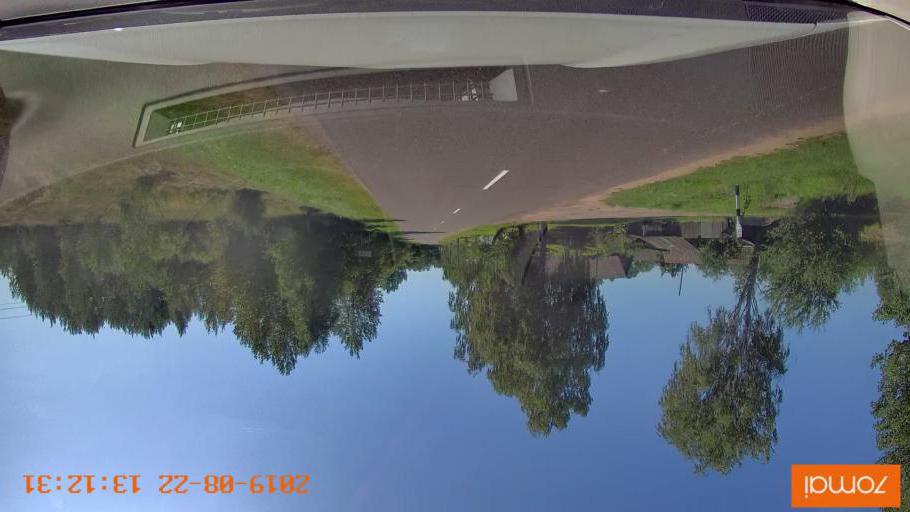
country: BY
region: Minsk
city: Prawdzinski
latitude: 53.2688
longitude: 27.8647
